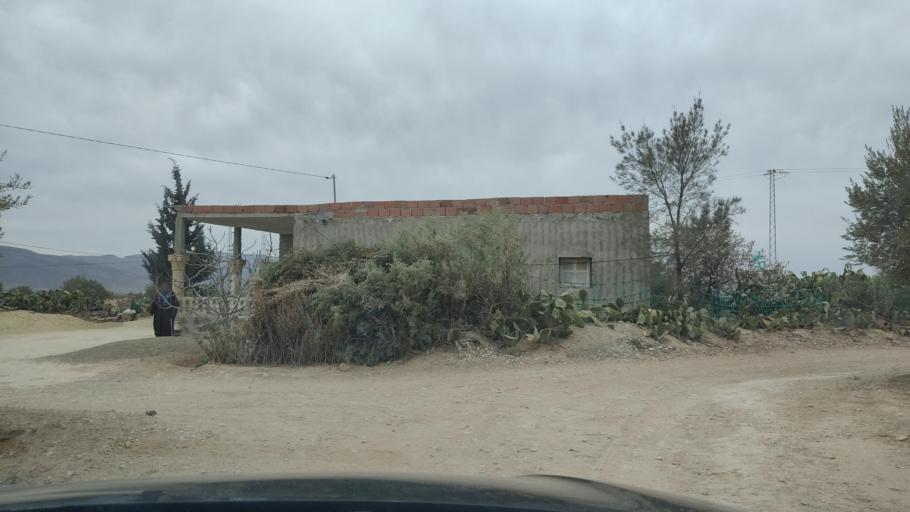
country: TN
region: Al Qasrayn
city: Kasserine
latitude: 35.2283
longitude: 8.9260
